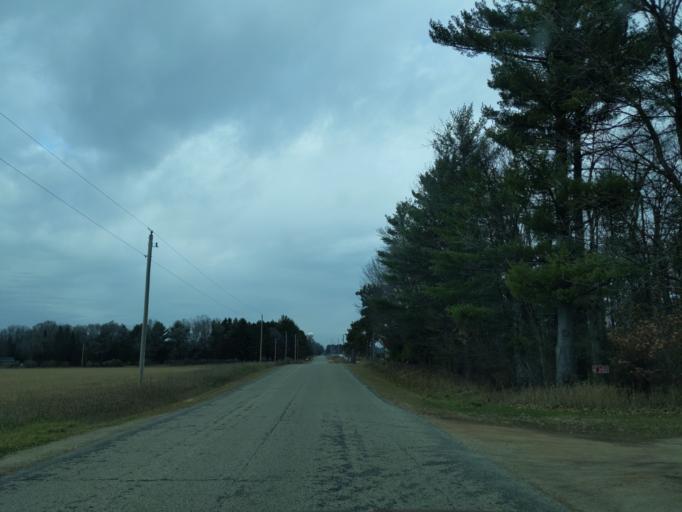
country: US
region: Wisconsin
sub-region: Waushara County
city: Wautoma
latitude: 44.0565
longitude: -89.2774
